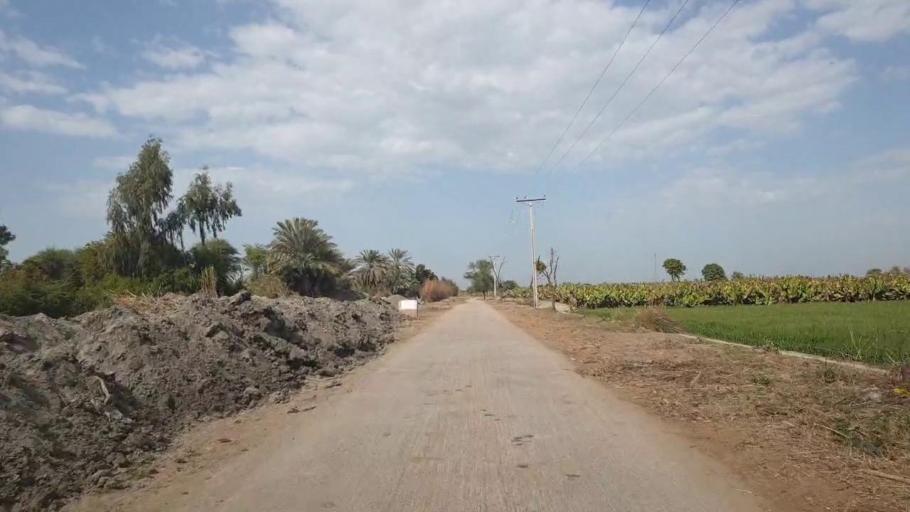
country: PK
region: Sindh
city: Shahdadpur
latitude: 25.9678
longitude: 68.4765
